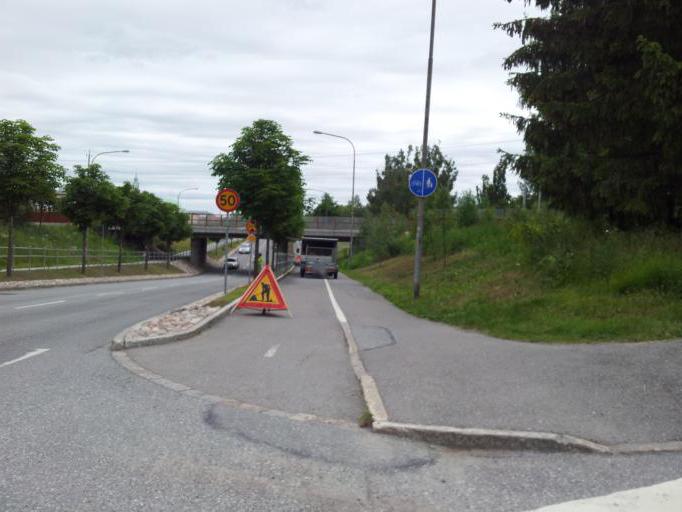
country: SE
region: Uppsala
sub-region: Uppsala Kommun
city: Uppsala
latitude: 59.8723
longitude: 17.6344
